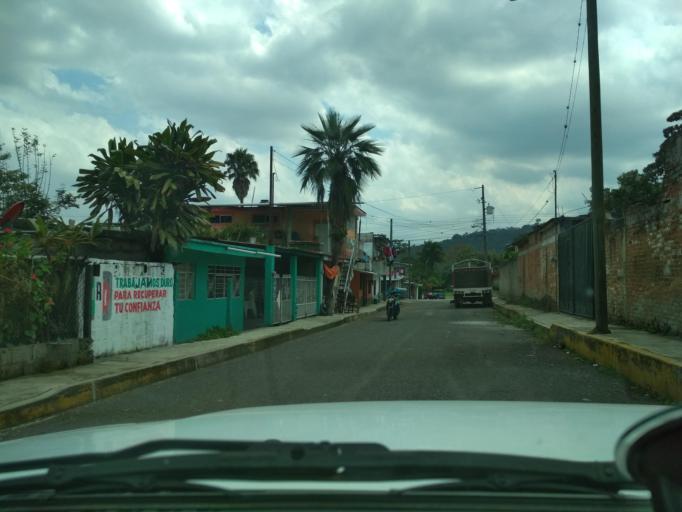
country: MX
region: Veracruz
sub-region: Fortin
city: Monte Salas
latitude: 18.9366
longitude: -97.0182
